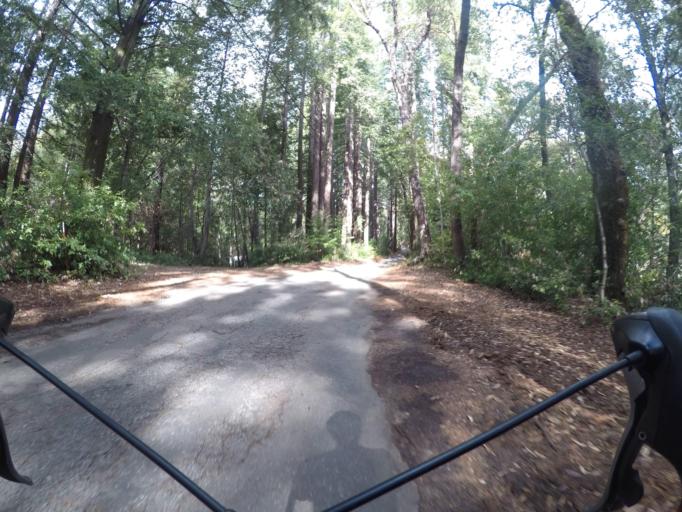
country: US
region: California
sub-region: Santa Cruz County
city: Ben Lomond
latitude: 37.1030
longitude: -122.0872
